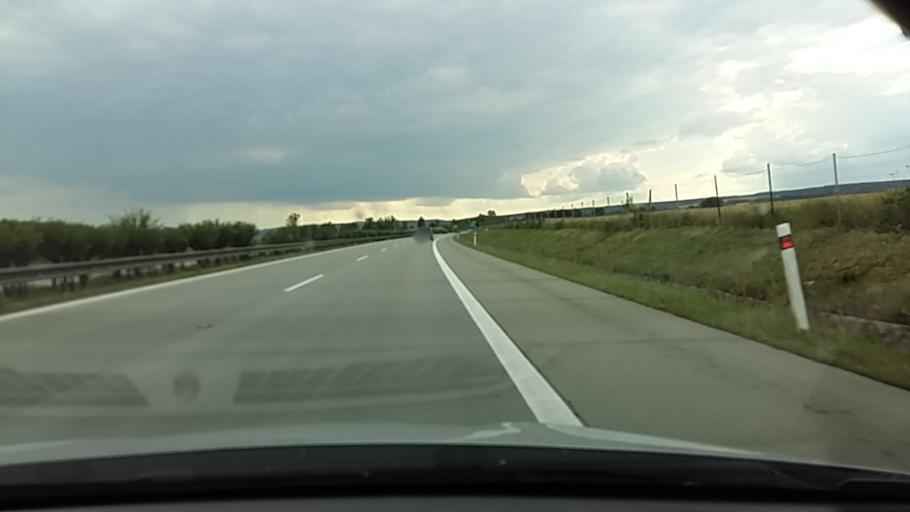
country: CZ
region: Plzensky
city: Hermanova Hut'
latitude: 49.7136
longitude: 13.1457
